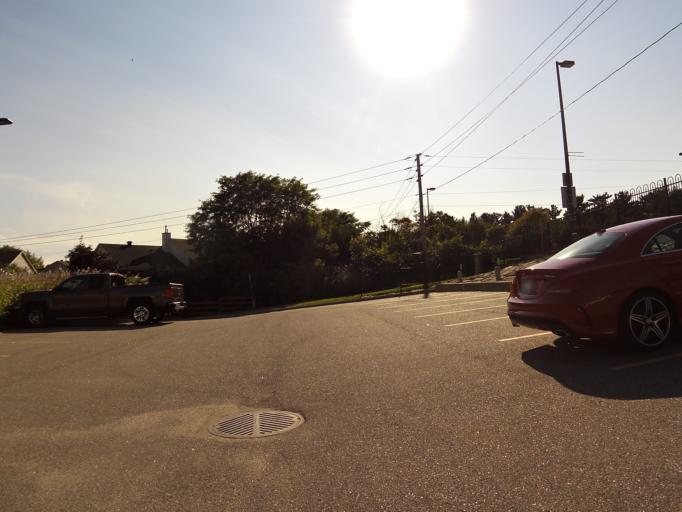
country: CA
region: Ontario
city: Ottawa
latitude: 45.4168
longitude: -75.7610
